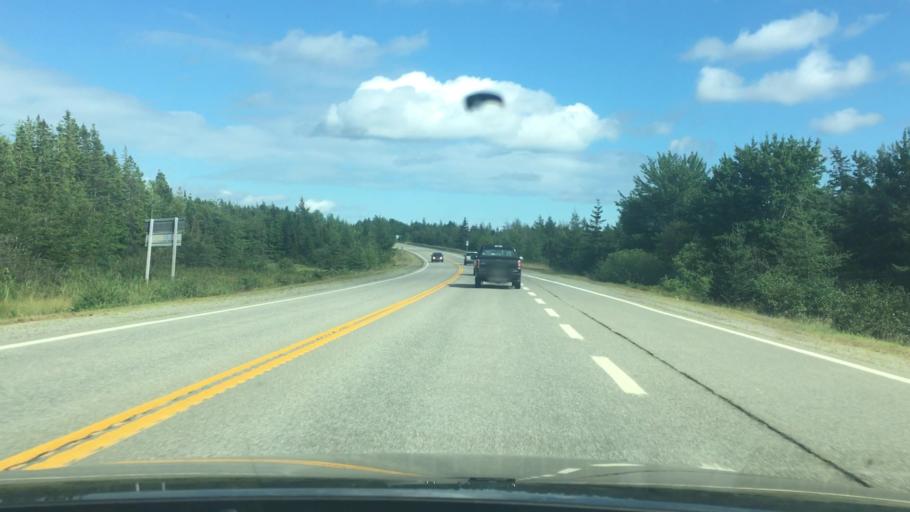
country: CA
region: Nova Scotia
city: Princeville
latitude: 45.6115
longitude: -61.0739
